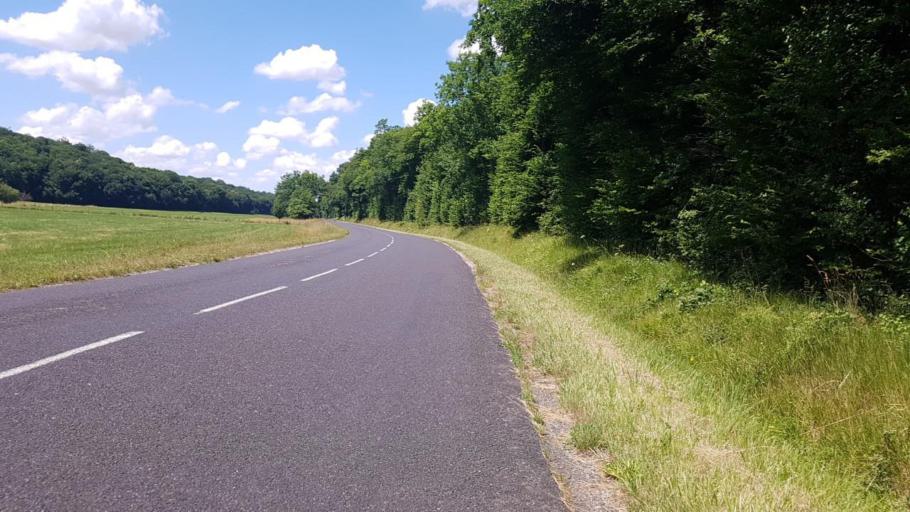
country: FR
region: Lorraine
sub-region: Departement de la Meuse
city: Vacon
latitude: 48.6727
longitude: 5.5794
